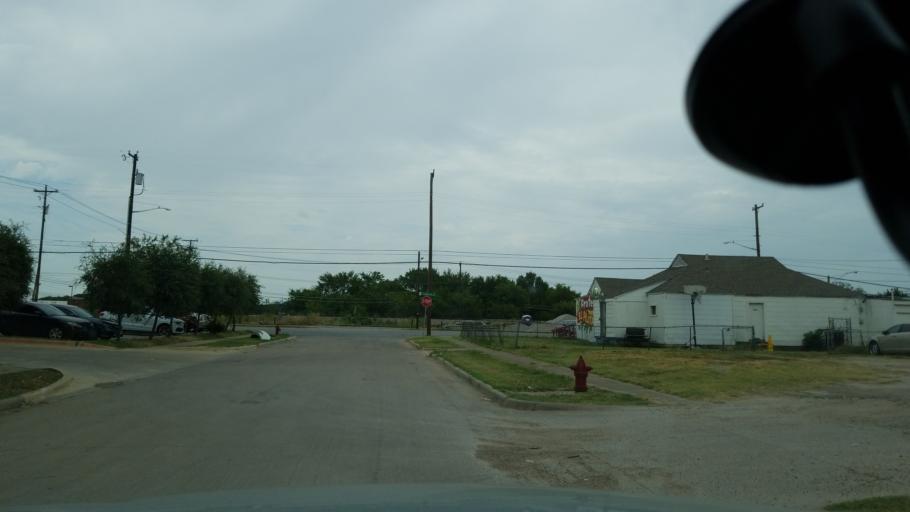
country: US
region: Texas
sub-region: Dallas County
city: Grand Prairie
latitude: 32.7442
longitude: -96.9919
